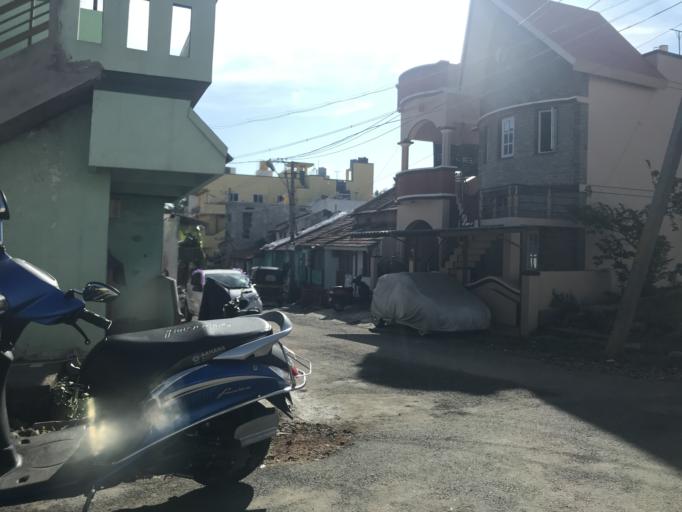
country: IN
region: Karnataka
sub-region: Mysore
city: Mysore
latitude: 12.2905
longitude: 76.6414
